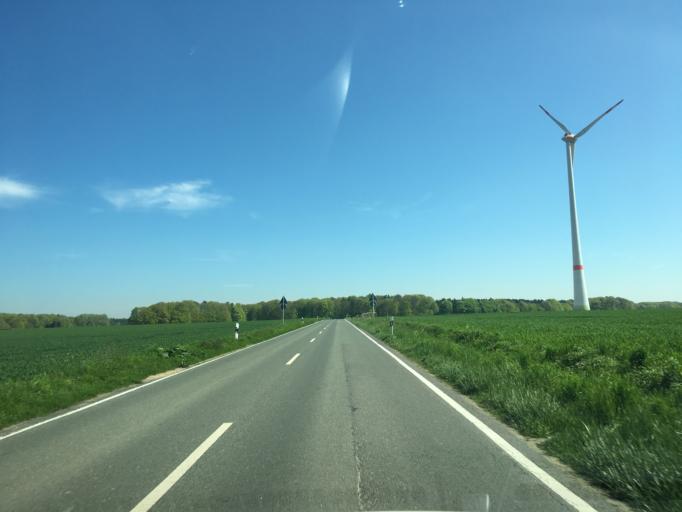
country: DE
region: North Rhine-Westphalia
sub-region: Regierungsbezirk Munster
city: Laer
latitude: 52.0358
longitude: 7.3194
